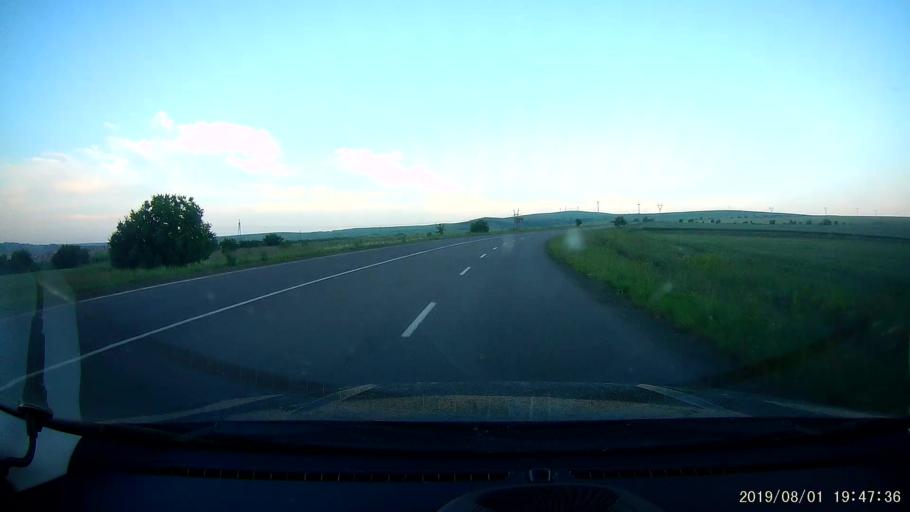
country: BG
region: Burgas
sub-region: Obshtina Karnobat
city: Karnobat
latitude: 42.6495
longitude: 26.9577
